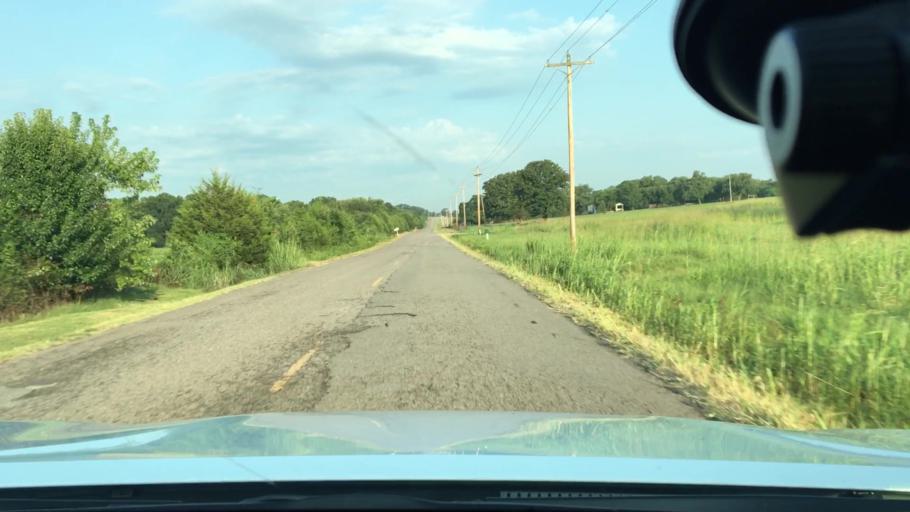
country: US
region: Arkansas
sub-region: Johnson County
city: Coal Hill
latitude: 35.3663
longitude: -93.6051
